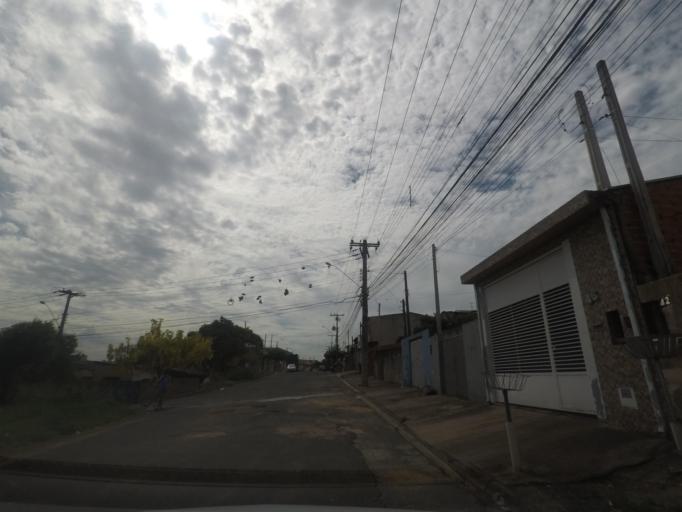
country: BR
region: Sao Paulo
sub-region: Sumare
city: Sumare
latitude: -22.8107
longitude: -47.2695
